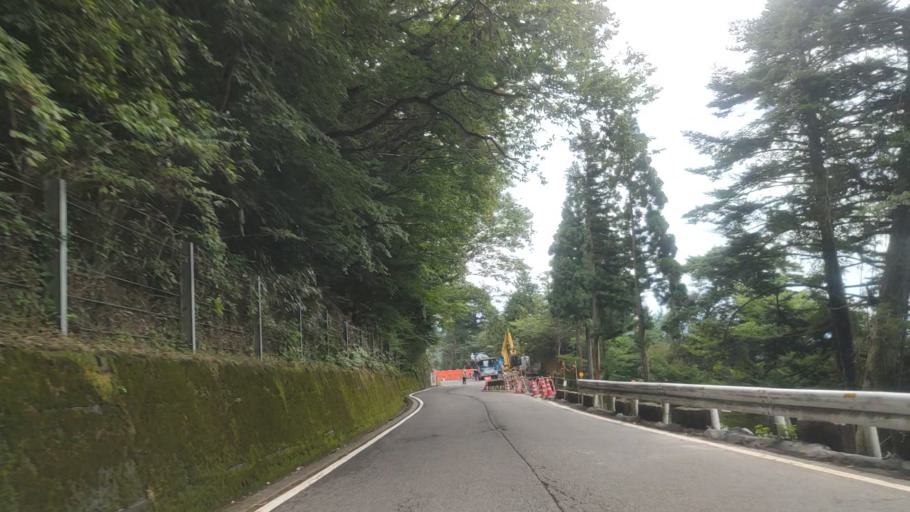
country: JP
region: Wakayama
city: Koya
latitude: 34.2164
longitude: 135.5715
